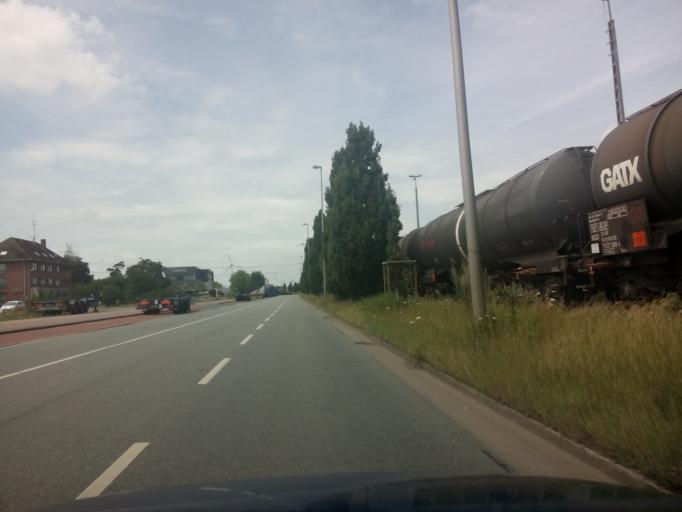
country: DE
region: Lower Saxony
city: Ritterhude
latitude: 53.1257
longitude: 8.7354
